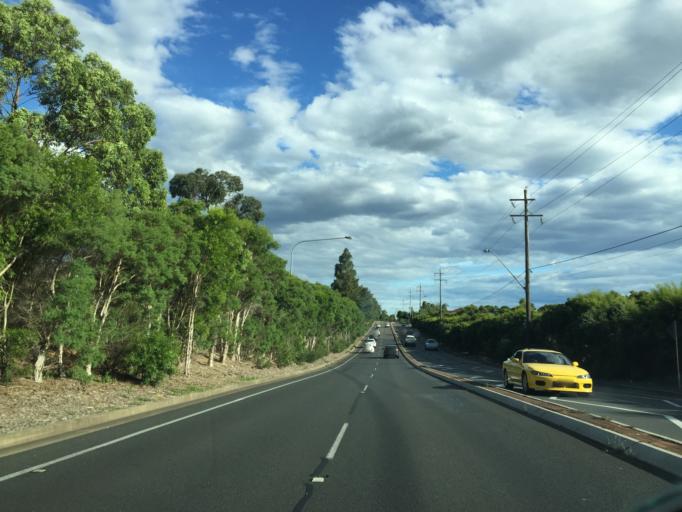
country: AU
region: New South Wales
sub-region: The Hills Shire
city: Glenhaven
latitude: -33.7064
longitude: 150.9728
